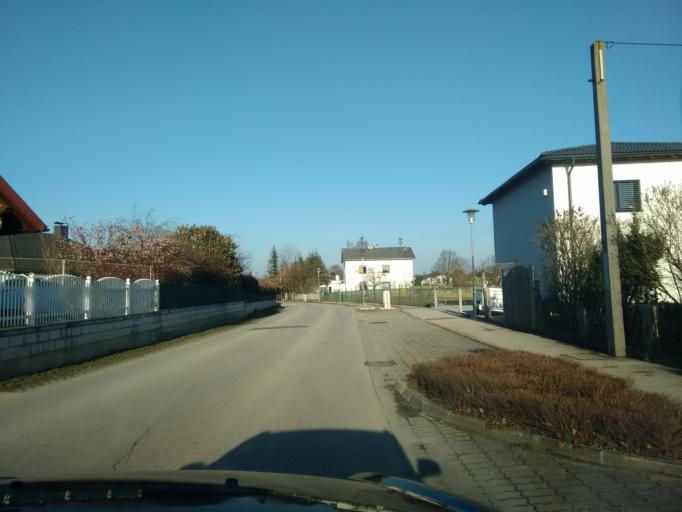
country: AT
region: Upper Austria
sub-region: Wels-Land
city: Marchtrenk
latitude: 48.1941
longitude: 14.0940
